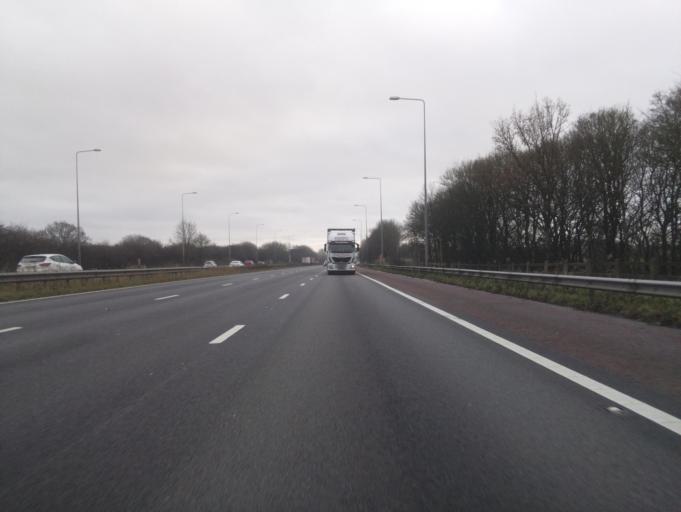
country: GB
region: England
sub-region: Lancashire
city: Coppull
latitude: 53.6256
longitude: -2.6879
